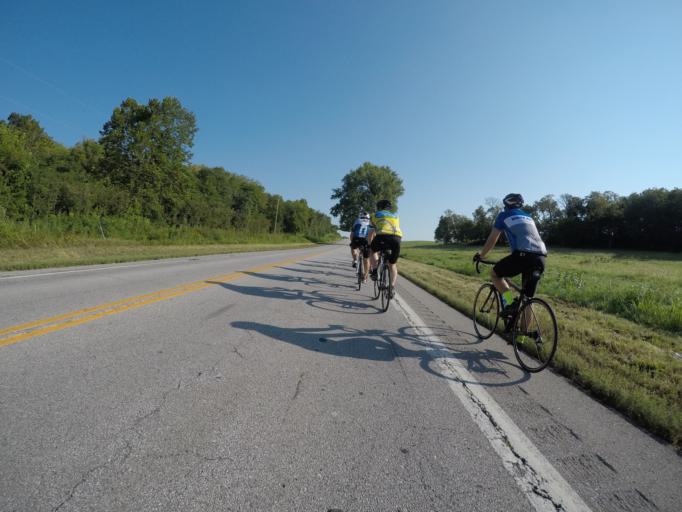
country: US
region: Missouri
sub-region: Platte County
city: Weston
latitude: 39.3876
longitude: -94.8645
